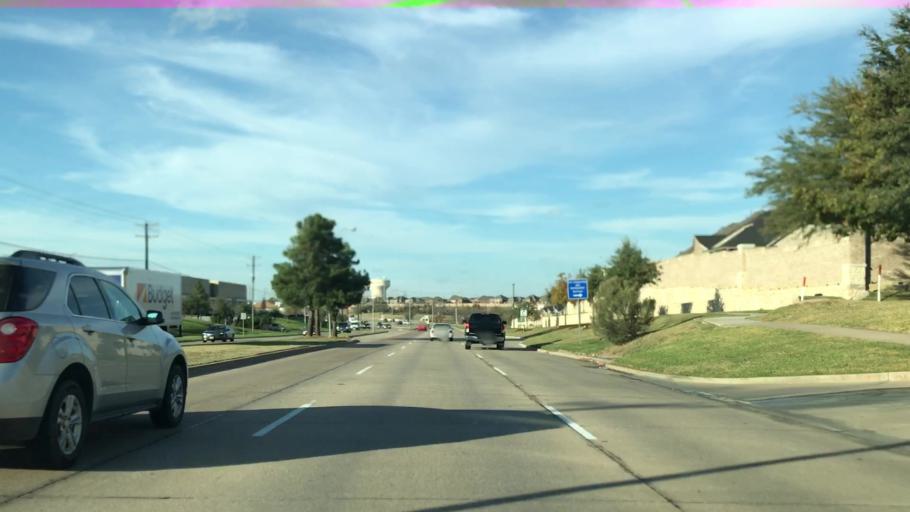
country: US
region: Texas
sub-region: Dallas County
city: Coppell
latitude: 32.8982
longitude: -96.9910
